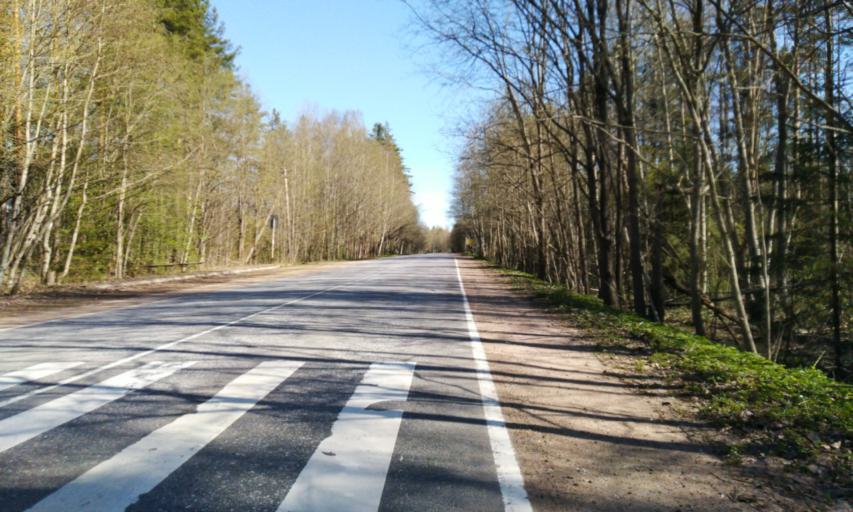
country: RU
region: Leningrad
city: Garbolovo
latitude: 60.3887
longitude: 30.4760
